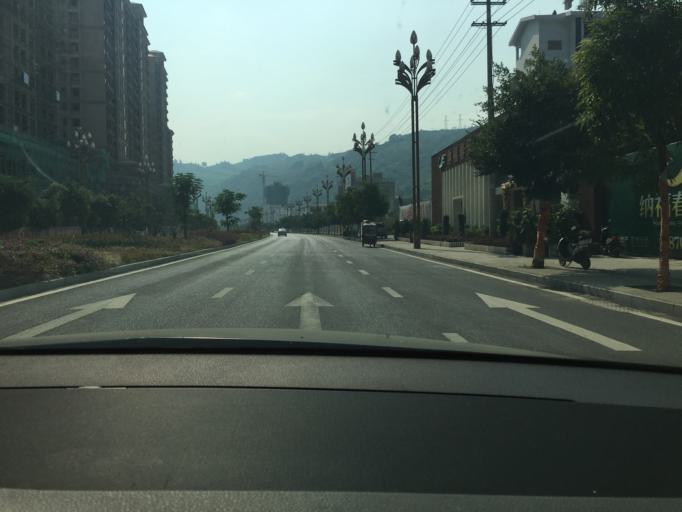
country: CN
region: Guangxi Zhuangzu Zizhiqu
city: Xinzhou
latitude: 24.9948
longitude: 105.7858
